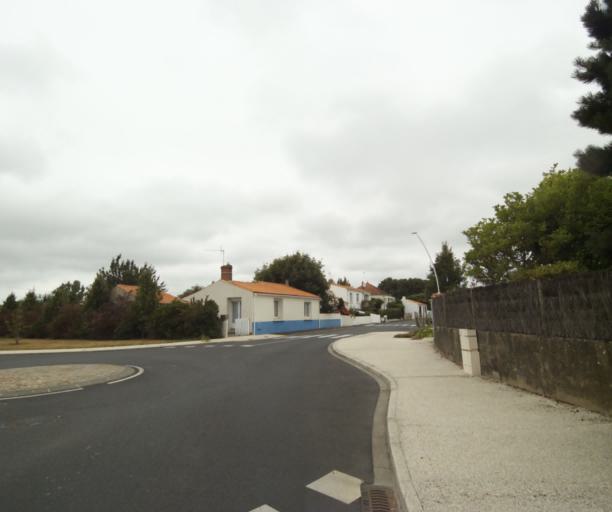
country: FR
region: Pays de la Loire
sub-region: Departement de la Vendee
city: Chateau-d'Olonne
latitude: 46.5060
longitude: -1.7413
